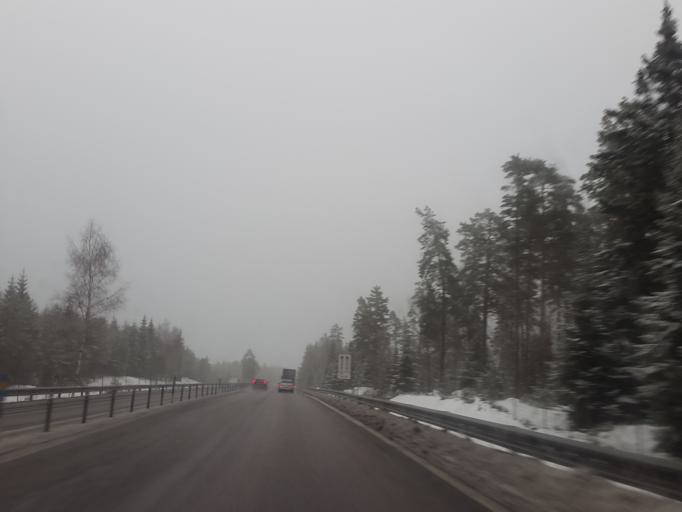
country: SE
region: Joenkoeping
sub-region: Jonkopings Kommun
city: Taberg
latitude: 57.7537
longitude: 13.9882
